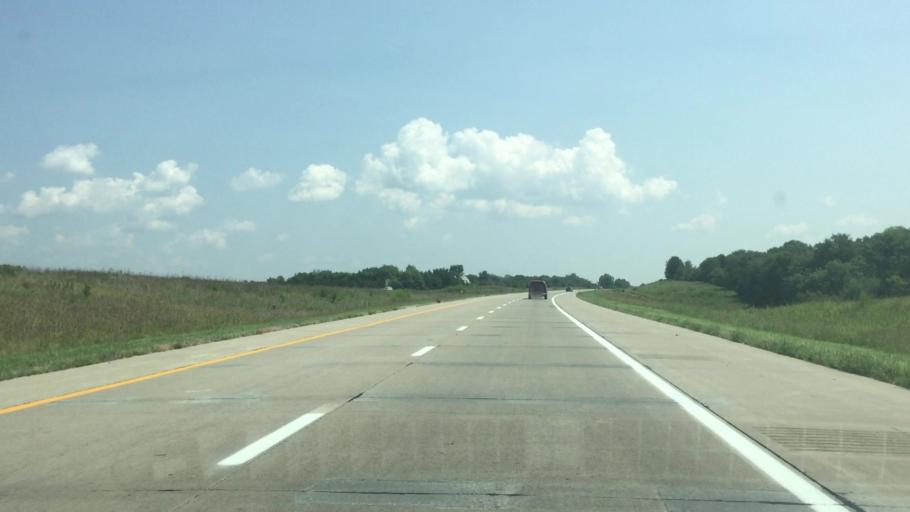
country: US
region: Kansas
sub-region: Franklin County
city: Ottawa
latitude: 38.5669
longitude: -95.2999
